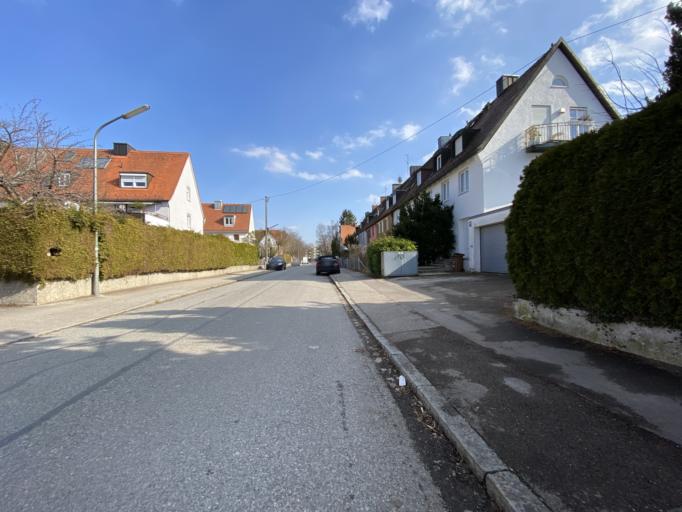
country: DE
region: Bavaria
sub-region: Upper Bavaria
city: Bogenhausen
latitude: 48.1585
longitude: 11.6335
